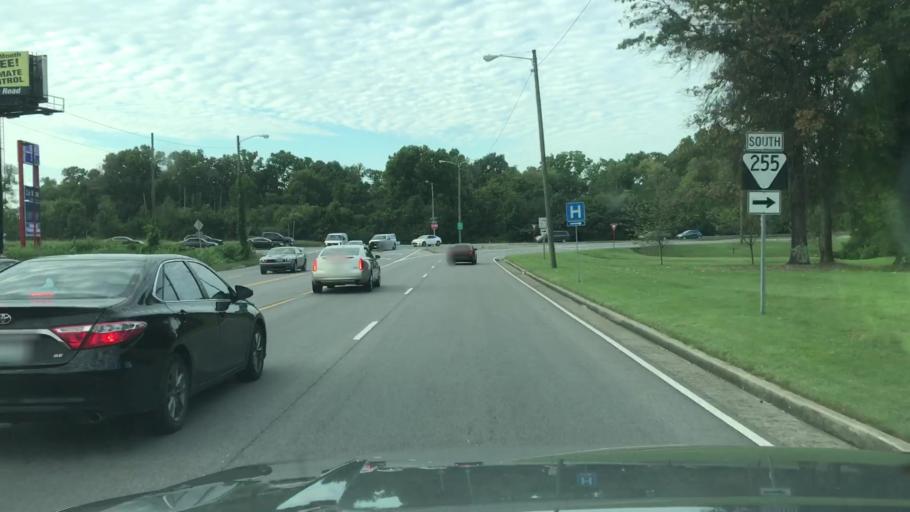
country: US
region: Tennessee
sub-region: Davidson County
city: Oak Hill
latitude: 36.0938
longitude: -86.6785
